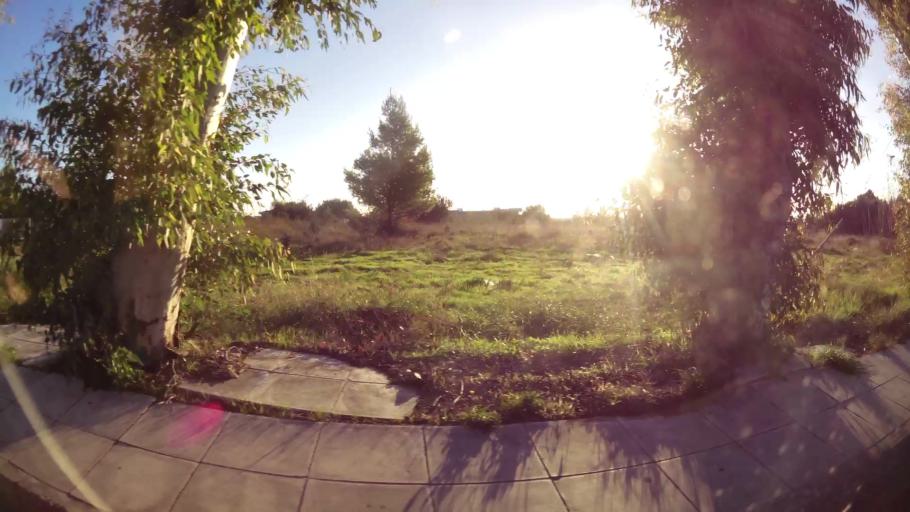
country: GR
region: Attica
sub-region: Nomarchia Anatolikis Attikis
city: Pallini
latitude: 37.9988
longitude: 23.8802
